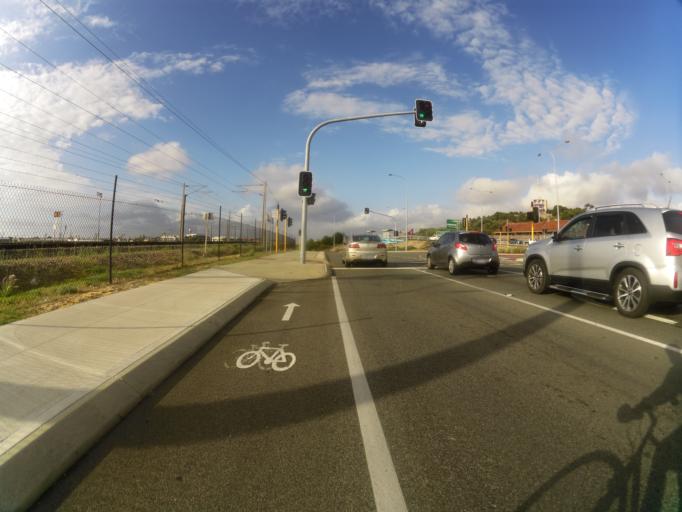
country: AU
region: Western Australia
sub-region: Fremantle
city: North Fremantle
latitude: -32.0441
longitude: 115.7528
